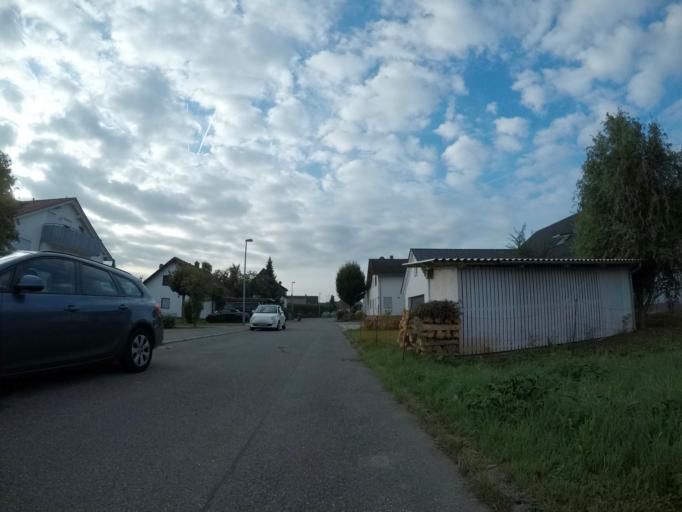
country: DE
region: Baden-Wuerttemberg
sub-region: Tuebingen Region
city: Sickenhausen
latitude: 48.5214
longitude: 9.1732
